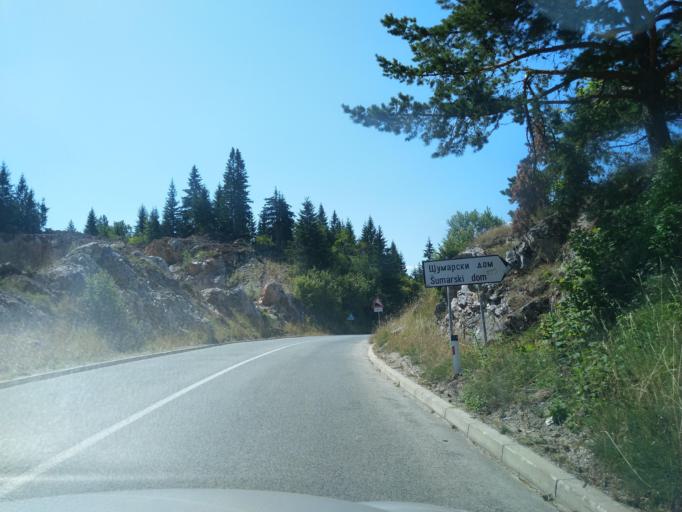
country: RS
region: Central Serbia
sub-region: Zlatiborski Okrug
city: Nova Varos
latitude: 43.4052
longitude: 19.8440
